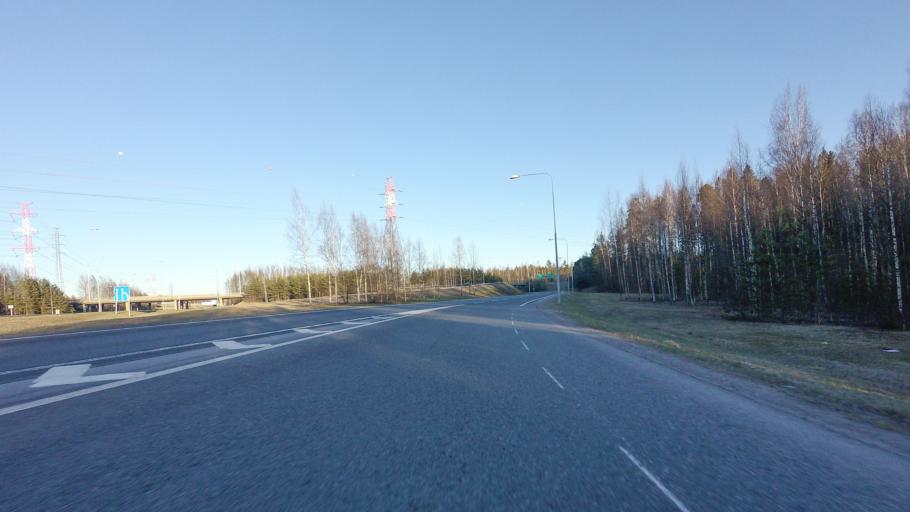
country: FI
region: Uusimaa
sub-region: Helsinki
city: Vantaa
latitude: 60.2748
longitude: 25.0838
